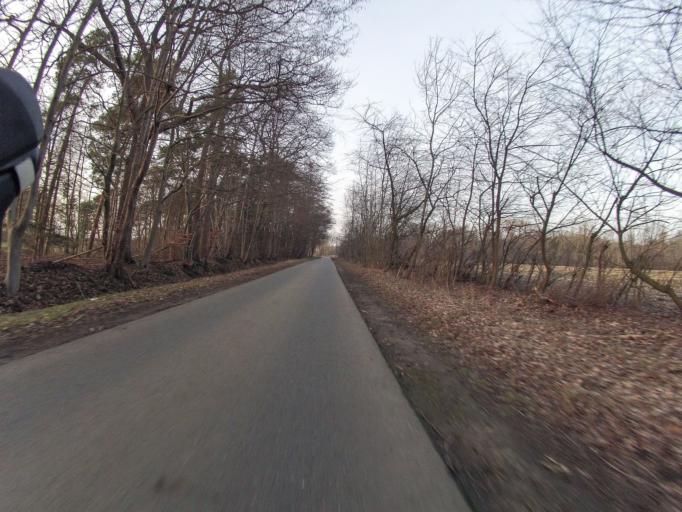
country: DE
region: North Rhine-Westphalia
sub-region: Regierungsbezirk Munster
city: Wettringen
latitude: 52.1812
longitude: 7.3319
